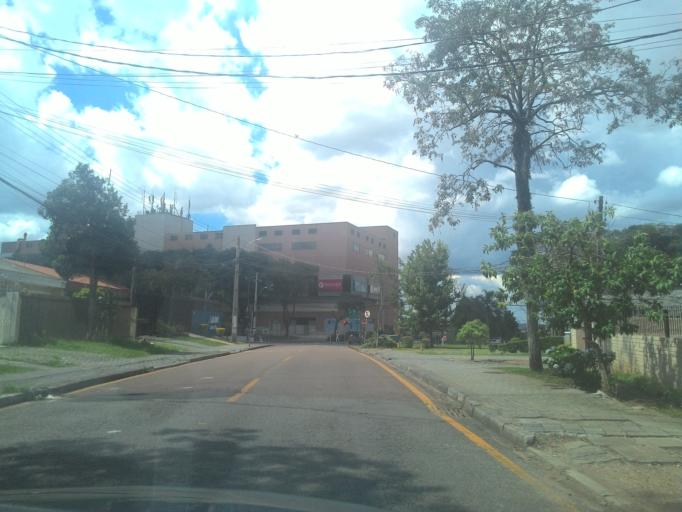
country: BR
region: Parana
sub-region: Pinhais
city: Pinhais
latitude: -25.4530
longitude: -49.2287
